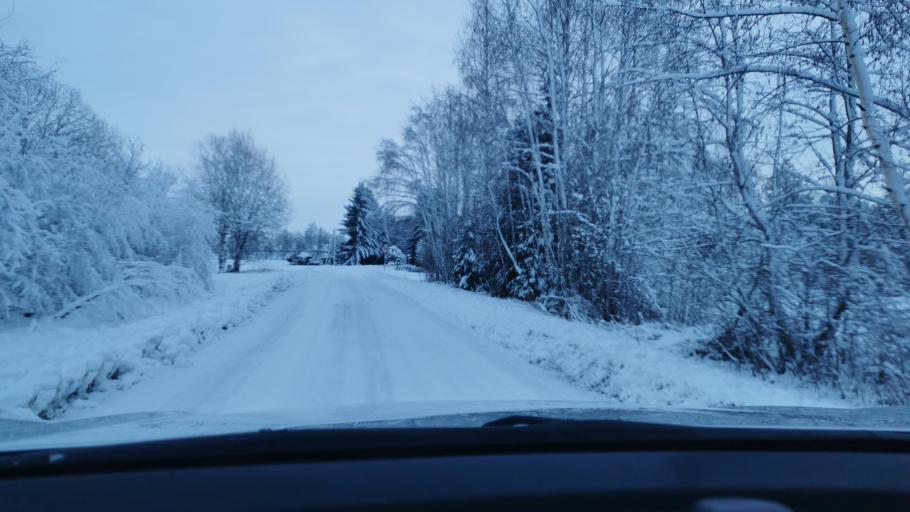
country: EE
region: Laeaene-Virumaa
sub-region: Haljala vald
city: Haljala
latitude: 59.5090
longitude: 26.2644
